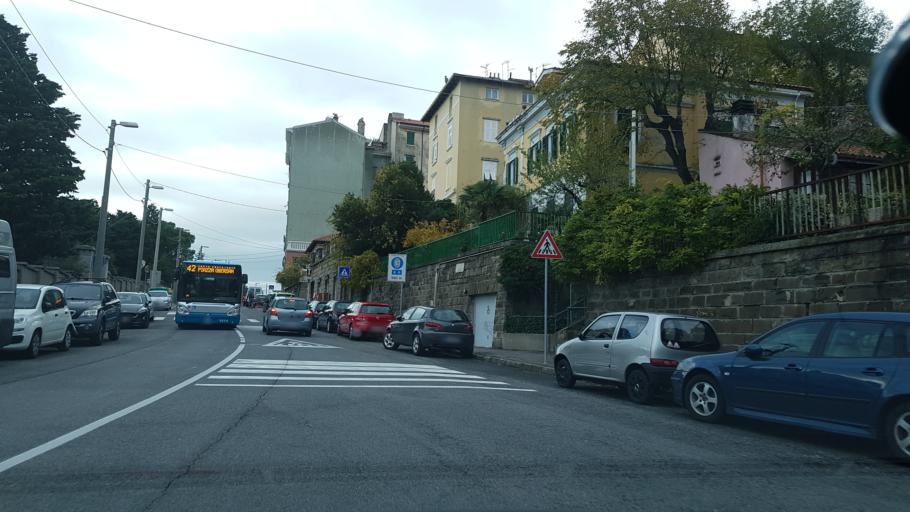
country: IT
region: Friuli Venezia Giulia
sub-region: Provincia di Trieste
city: Villa Opicina
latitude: 45.6696
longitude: 13.7635
